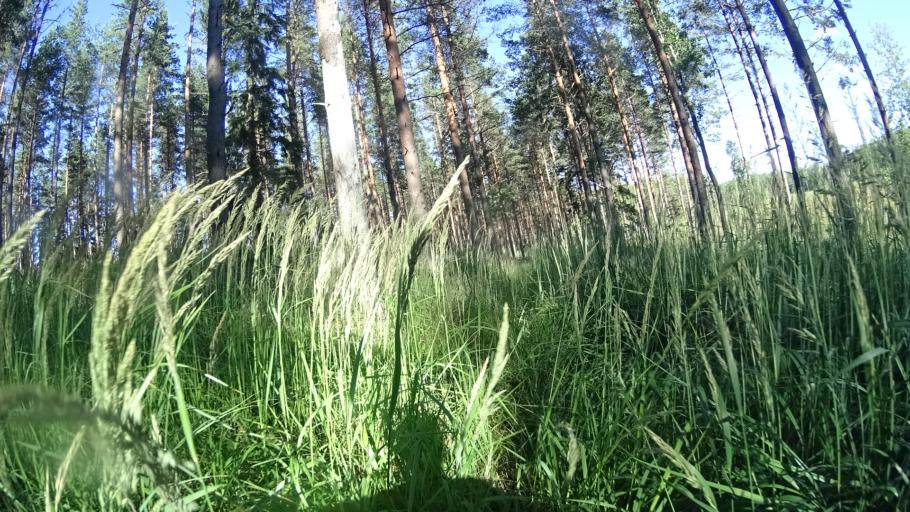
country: FI
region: Uusimaa
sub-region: Helsinki
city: Karkkila
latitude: 60.6507
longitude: 24.1551
